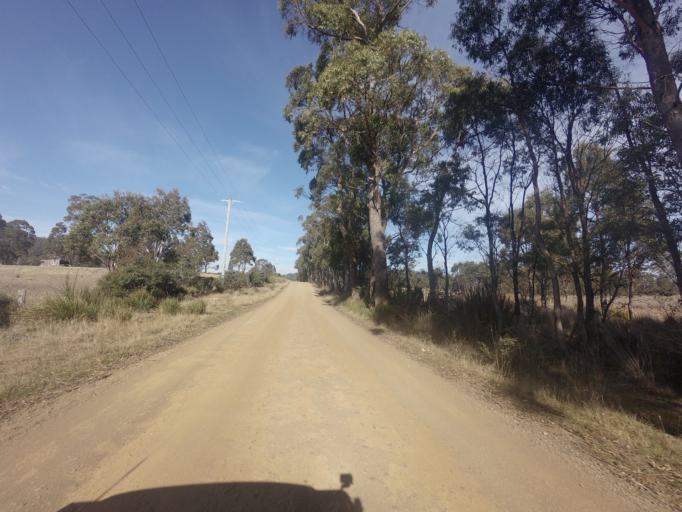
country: AU
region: Tasmania
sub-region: Sorell
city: Sorell
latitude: -42.4909
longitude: 147.5226
